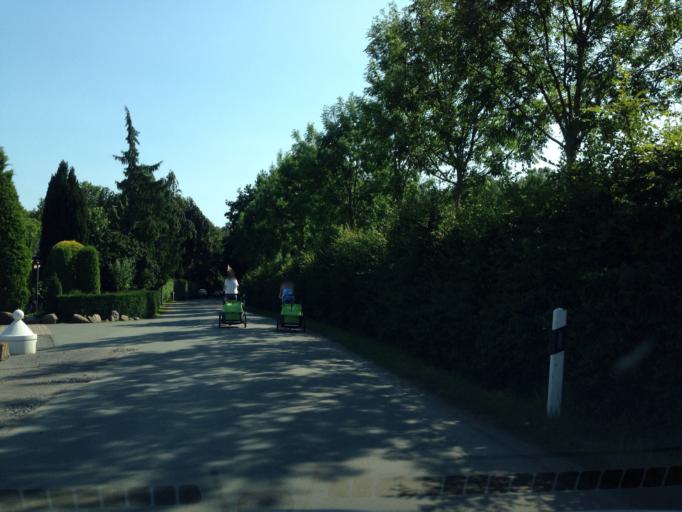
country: DE
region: North Rhine-Westphalia
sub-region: Regierungsbezirk Munster
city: Muenster
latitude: 51.9795
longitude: 7.6221
